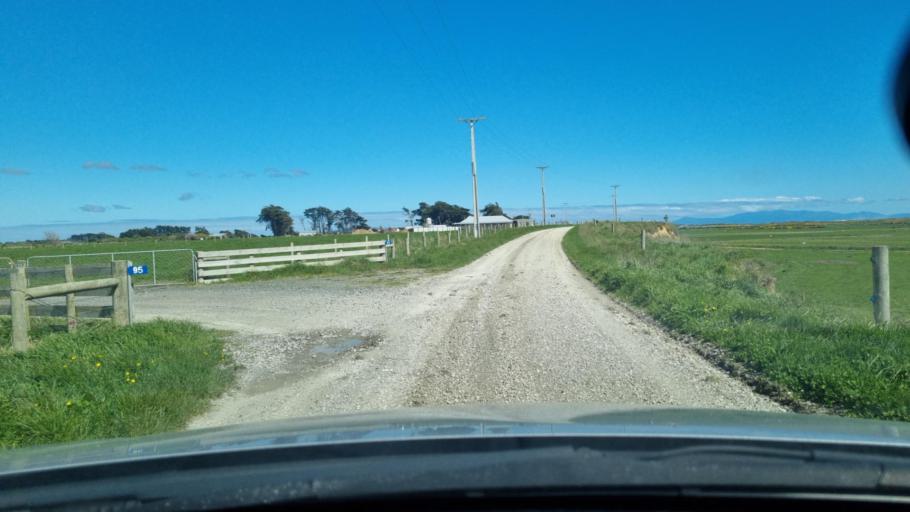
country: NZ
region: Southland
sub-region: Invercargill City
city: Invercargill
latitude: -46.3975
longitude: 168.2575
